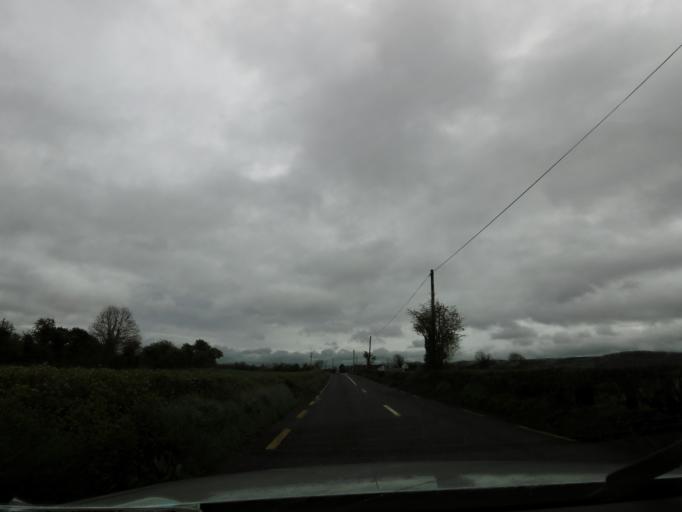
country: IE
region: Leinster
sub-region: Laois
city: Rathdowney
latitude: 52.7202
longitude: -7.5022
